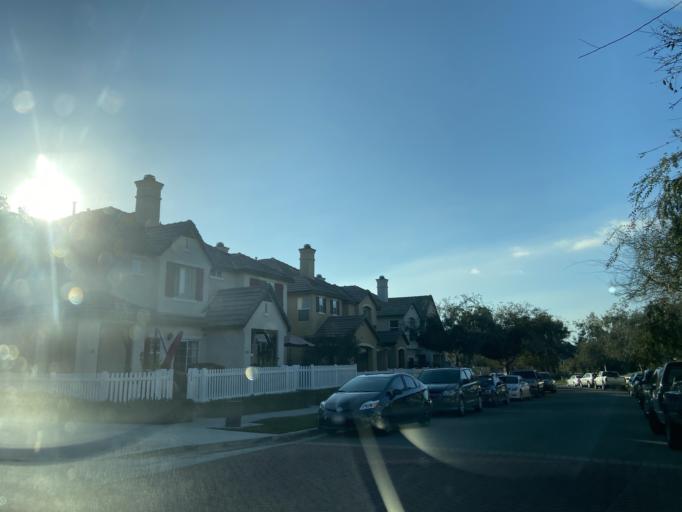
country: US
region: California
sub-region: San Diego County
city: Bonita
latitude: 32.6313
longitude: -116.9735
